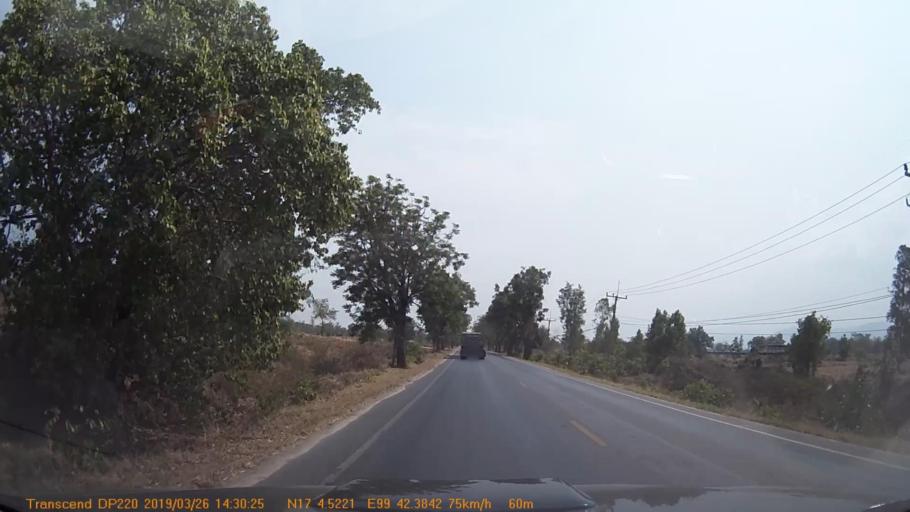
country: TH
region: Sukhothai
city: Ban Na
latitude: 17.0751
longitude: 99.7064
